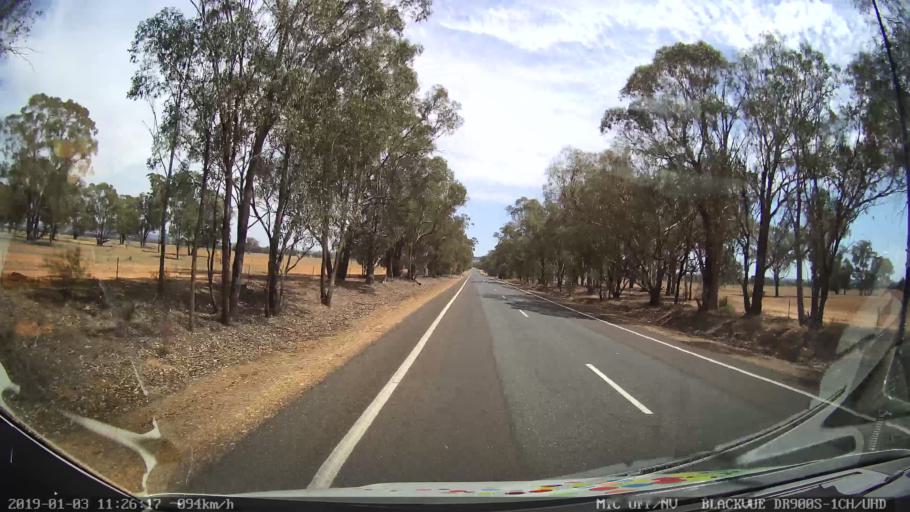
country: AU
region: New South Wales
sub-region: Weddin
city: Grenfell
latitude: -34.0271
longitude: 148.2261
